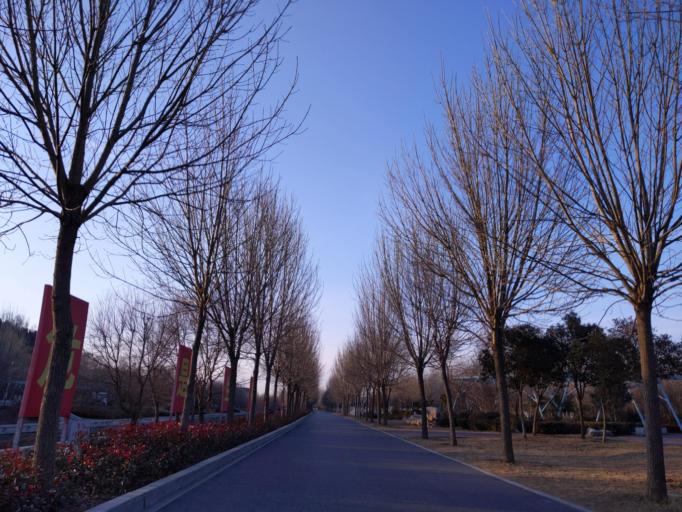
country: CN
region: Henan Sheng
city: Puyang
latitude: 35.7669
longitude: 115.0010
